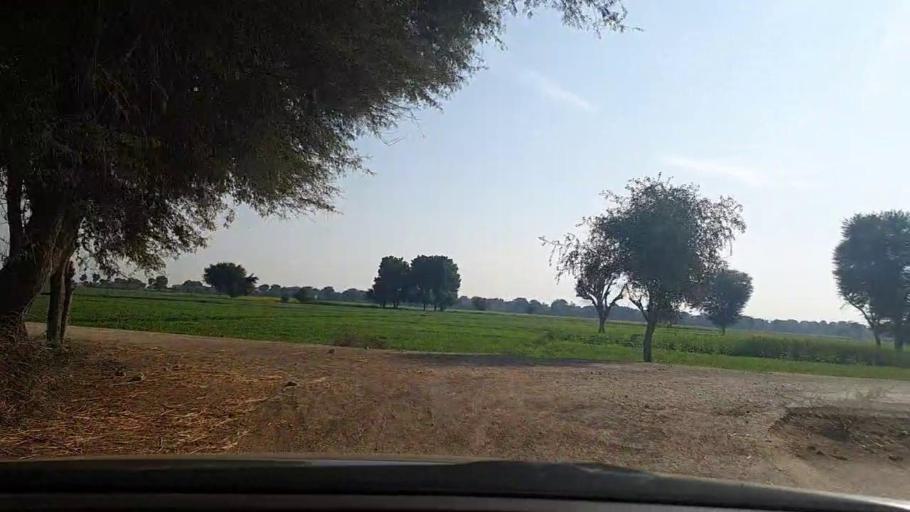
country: PK
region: Sindh
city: Sehwan
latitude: 26.3048
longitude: 68.0018
